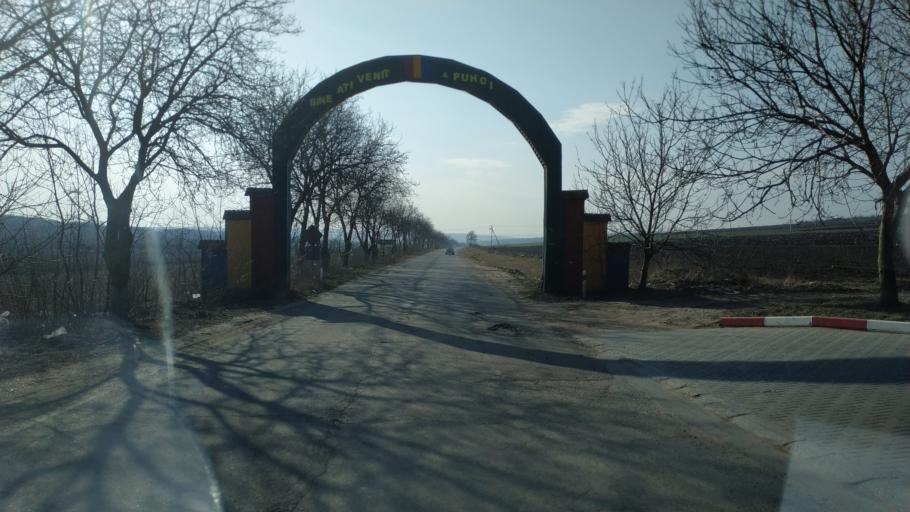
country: MD
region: Chisinau
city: Singera
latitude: 46.8557
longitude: 29.0211
